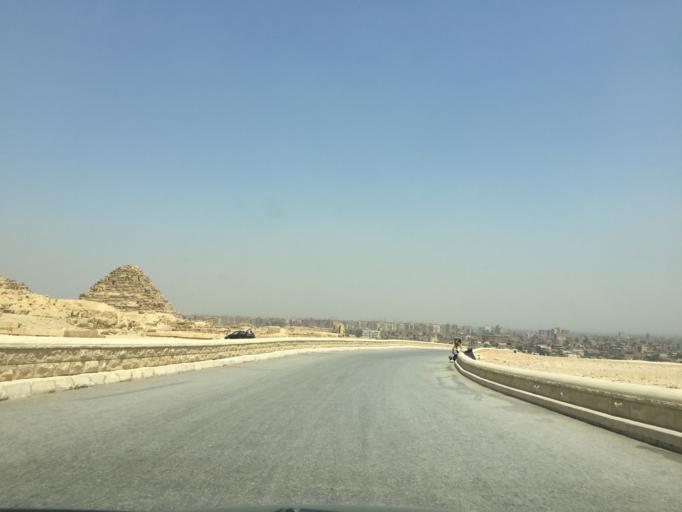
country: EG
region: Al Jizah
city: Al Jizah
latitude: 29.9774
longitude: 31.1338
